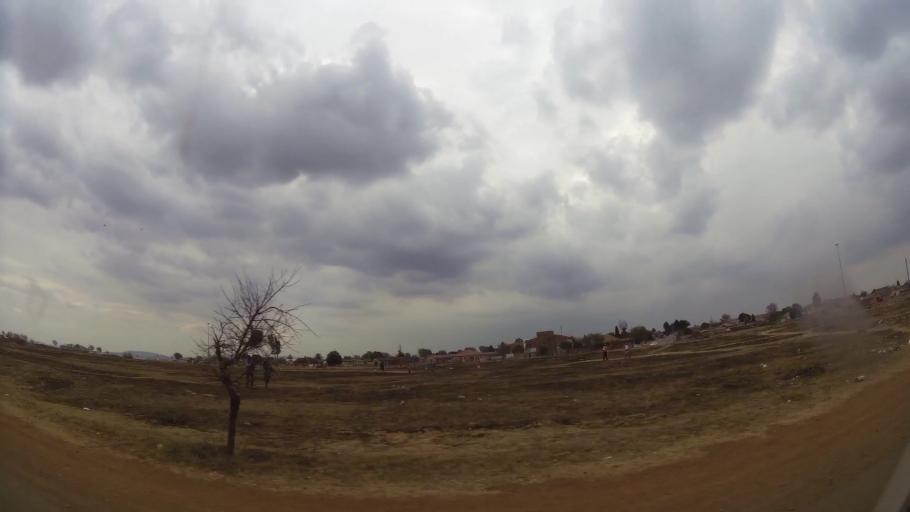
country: ZA
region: Gauteng
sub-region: Ekurhuleni Metropolitan Municipality
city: Germiston
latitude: -26.3836
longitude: 28.1364
